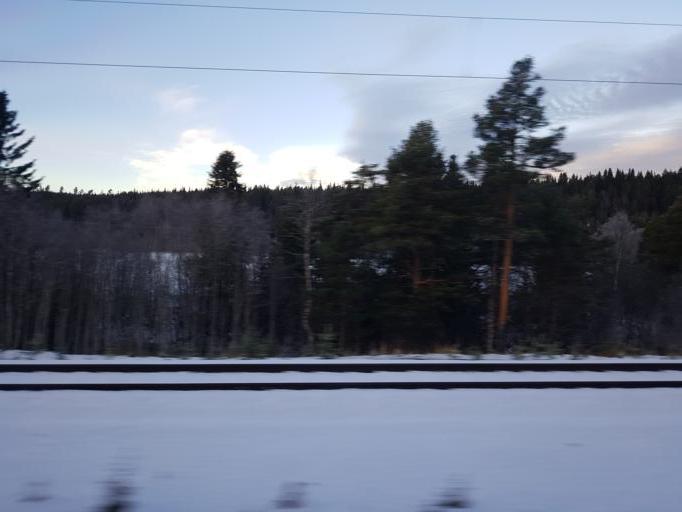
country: NO
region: Sor-Trondelag
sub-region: Rennebu
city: Berkak
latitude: 62.8824
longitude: 10.0930
